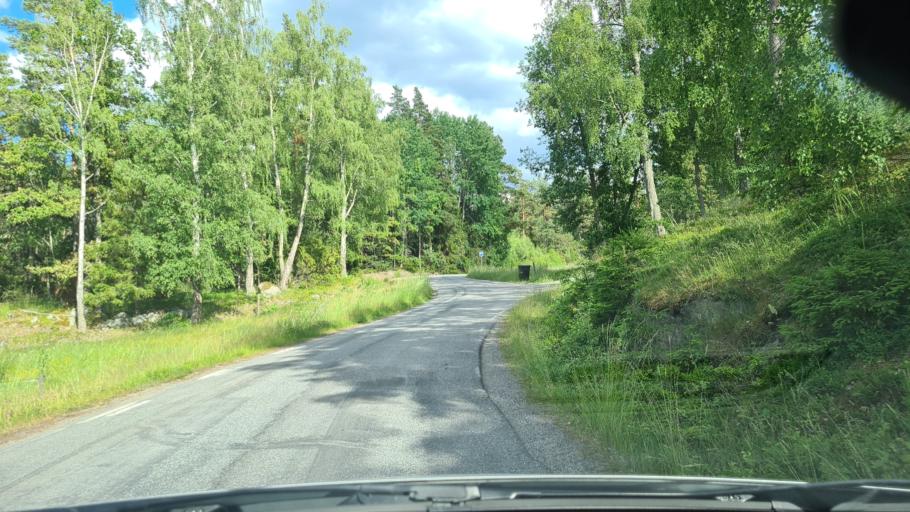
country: SE
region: Stockholm
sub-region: Vaxholms Kommun
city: Vaxholm
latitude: 59.4134
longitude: 18.4422
